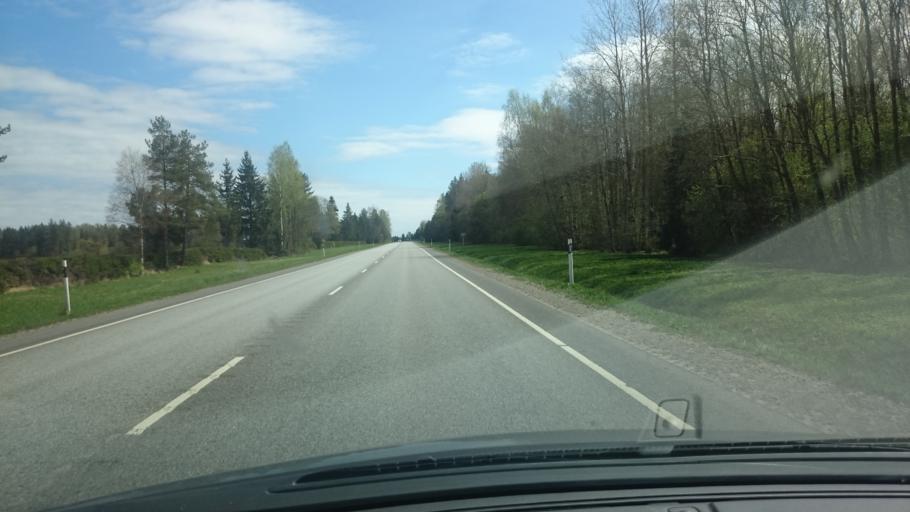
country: EE
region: Laeaene-Virumaa
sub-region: Someru vald
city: Someru
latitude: 59.3685
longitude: 26.5405
